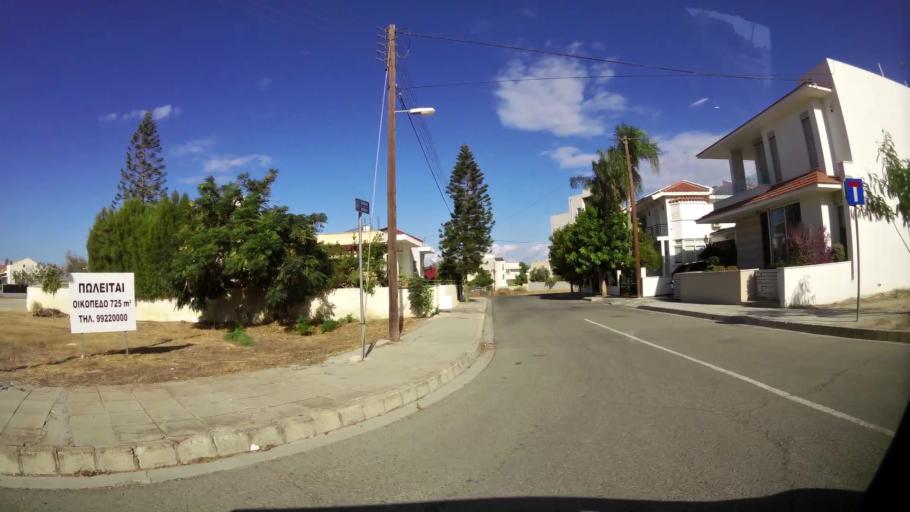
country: CY
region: Lefkosia
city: Nicosia
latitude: 35.1306
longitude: 33.3494
